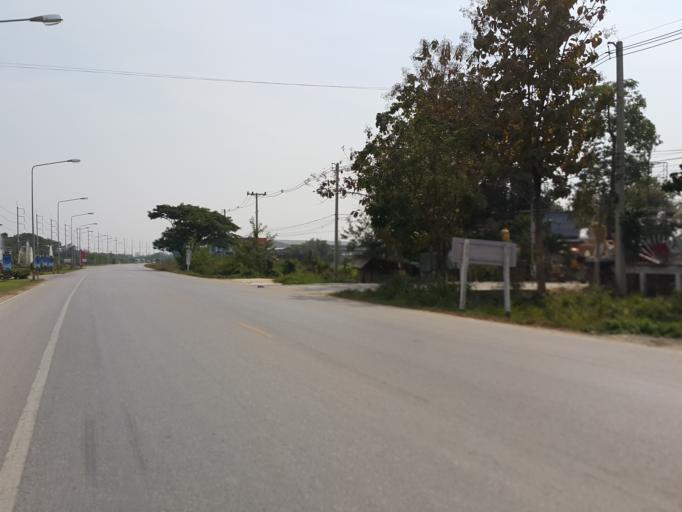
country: TH
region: Chiang Mai
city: San Sai
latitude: 18.7894
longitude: 99.0691
